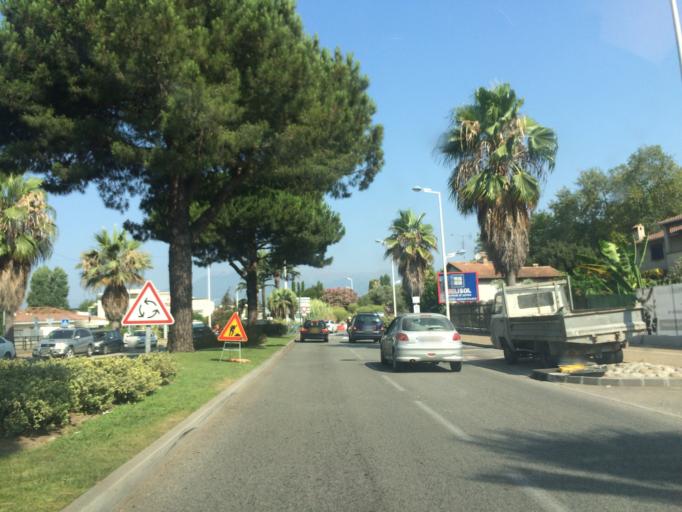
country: FR
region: Provence-Alpes-Cote d'Azur
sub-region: Departement des Alpes-Maritimes
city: Villeneuve-Loubet
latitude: 43.6619
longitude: 7.1328
